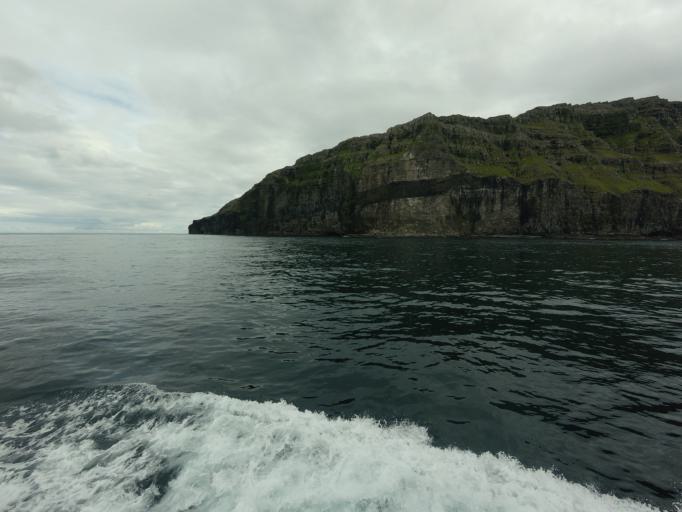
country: FO
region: Nordoyar
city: Klaksvik
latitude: 62.3076
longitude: -6.3496
